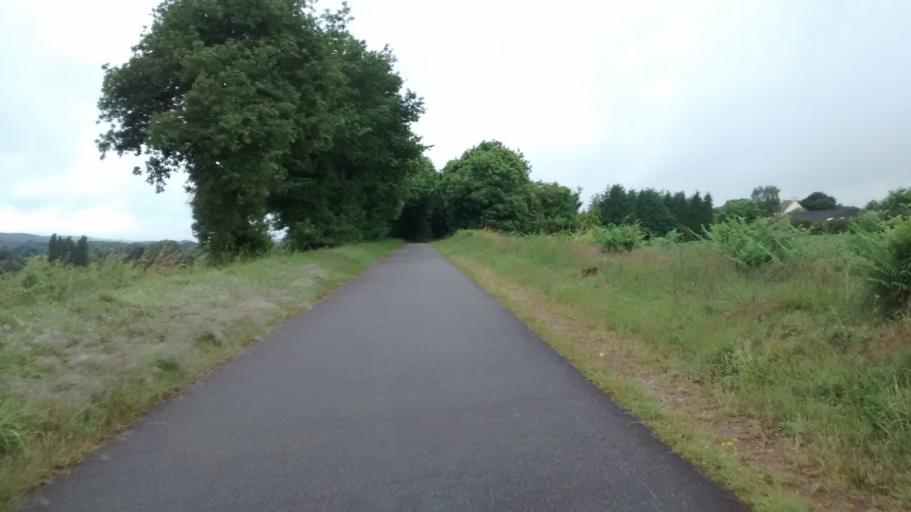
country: FR
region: Brittany
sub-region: Departement du Morbihan
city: Malestroit
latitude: 47.7889
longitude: -2.4006
